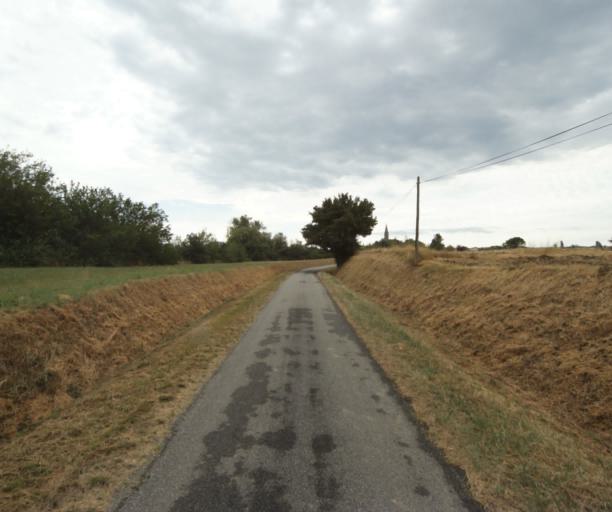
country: FR
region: Midi-Pyrenees
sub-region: Departement de la Haute-Garonne
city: Revel
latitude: 43.4383
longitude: 1.9631
